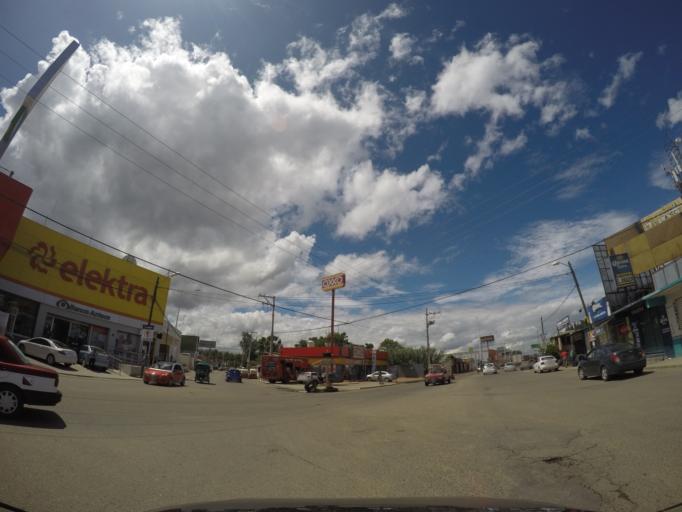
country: MX
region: Oaxaca
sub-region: Santa Cruz Xoxocotlan
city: Santa Cruz Xoxocotlan
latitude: 17.0231
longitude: -96.7301
